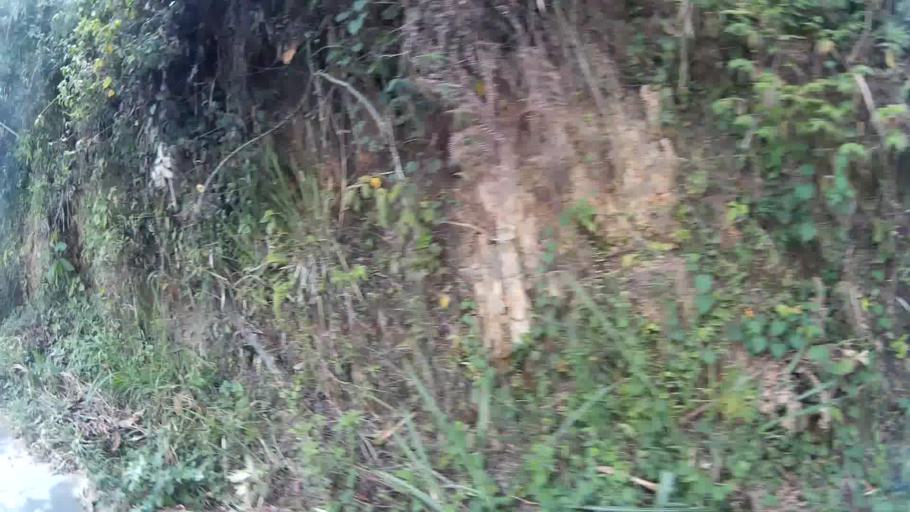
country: CO
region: Risaralda
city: Marsella
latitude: 4.8843
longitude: -75.7582
